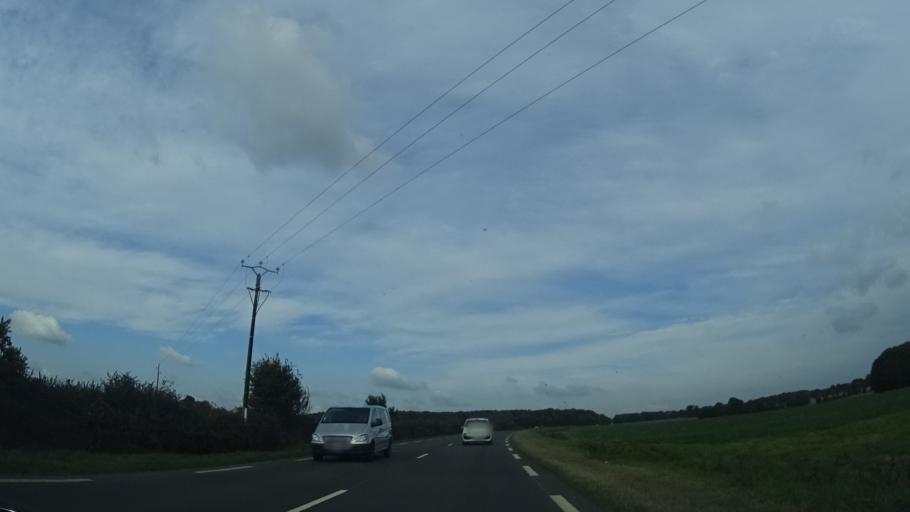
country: FR
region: Brittany
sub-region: Departement d'Ille-et-Vilaine
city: Hede-Bazouges
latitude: 48.3320
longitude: -1.7923
